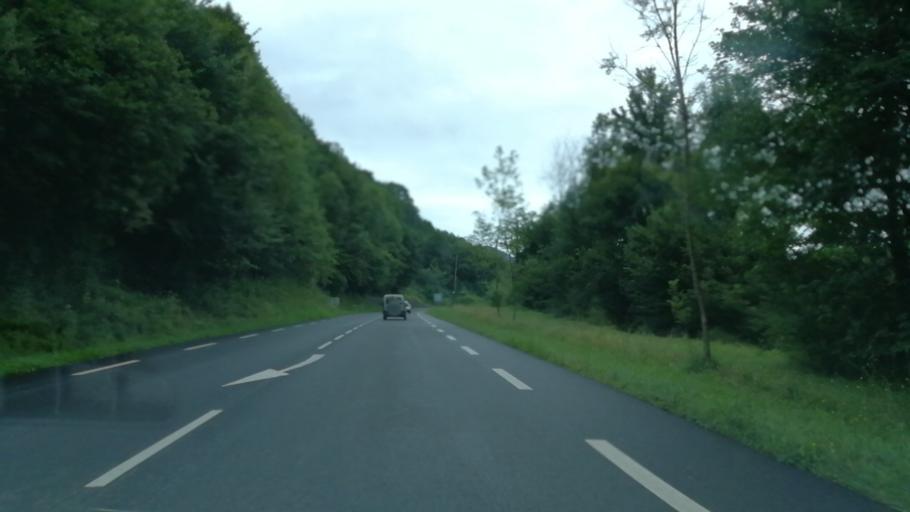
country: FR
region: Aquitaine
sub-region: Departement des Pyrenees-Atlantiques
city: Arette
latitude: 43.0824
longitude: -0.6145
